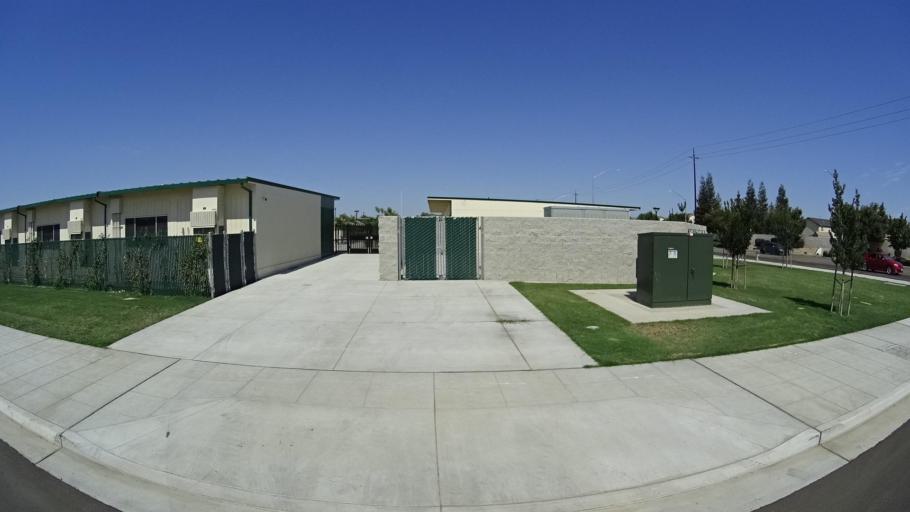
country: US
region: California
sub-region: Fresno County
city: Sunnyside
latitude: 36.7145
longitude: -119.7125
